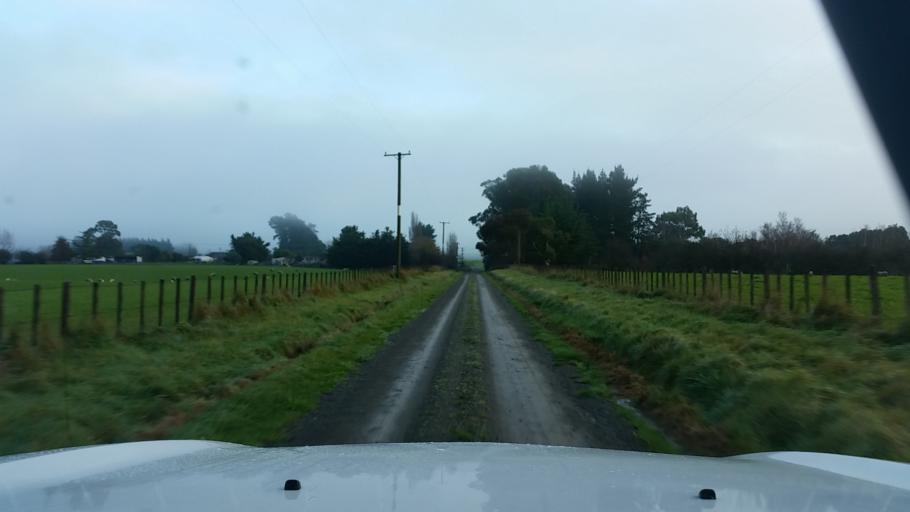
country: NZ
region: Wellington
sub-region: Masterton District
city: Masterton
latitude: -41.0800
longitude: 175.6592
